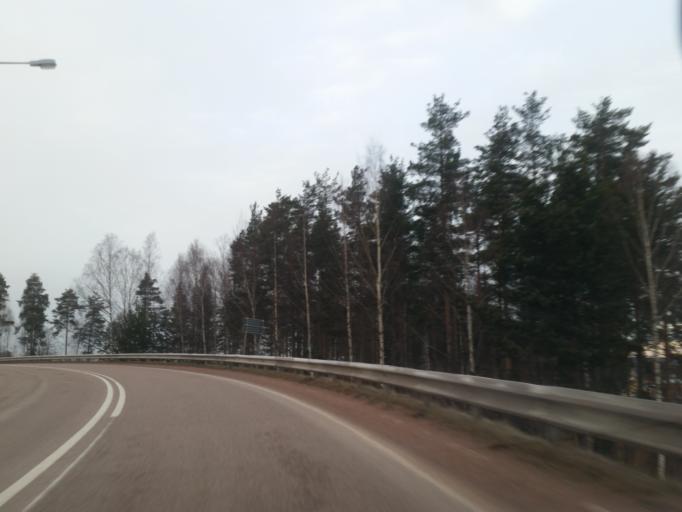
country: SE
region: Dalarna
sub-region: Leksand Municipality
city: Leksand
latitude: 60.7203
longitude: 15.0216
